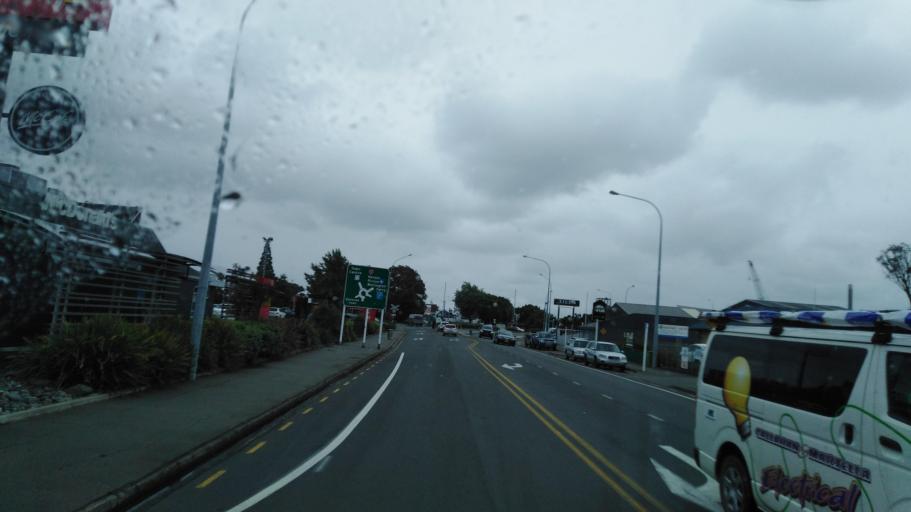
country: NZ
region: Marlborough
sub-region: Marlborough District
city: Blenheim
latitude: -41.5134
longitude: 173.9615
